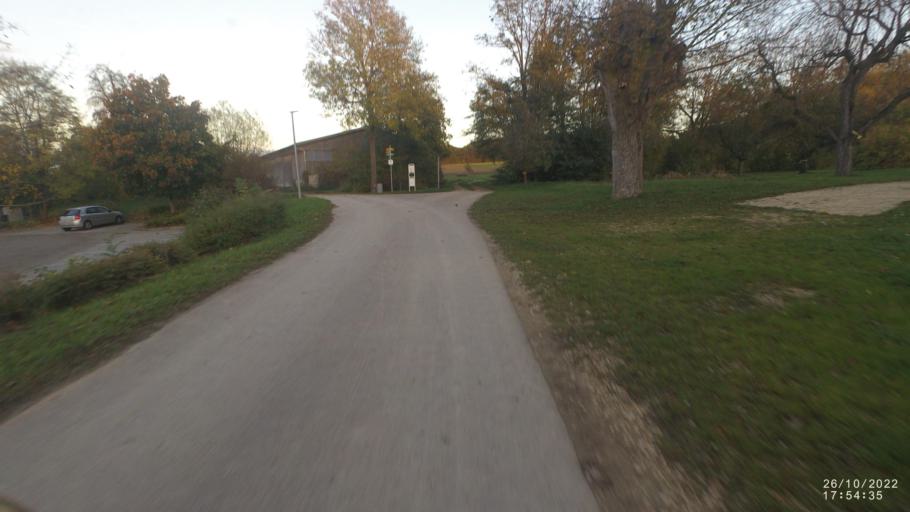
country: DE
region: Baden-Wuerttemberg
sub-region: Regierungsbezirk Stuttgart
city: Eschenbach
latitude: 48.6578
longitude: 9.6739
